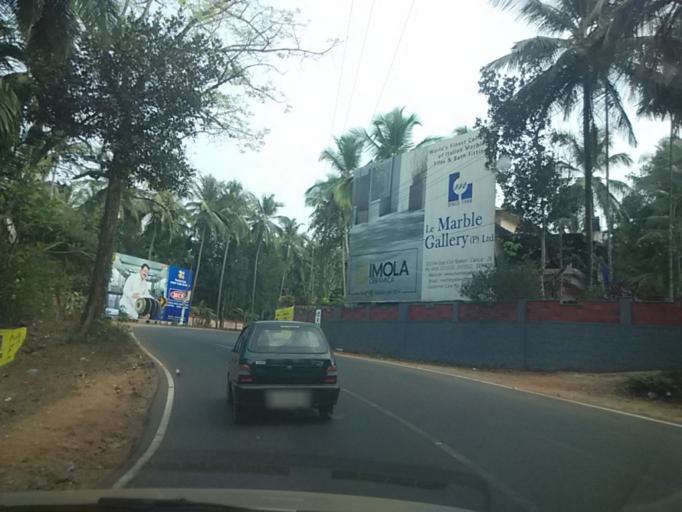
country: IN
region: Kerala
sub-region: Kozhikode
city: Naduvannur
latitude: 11.4958
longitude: 75.7739
